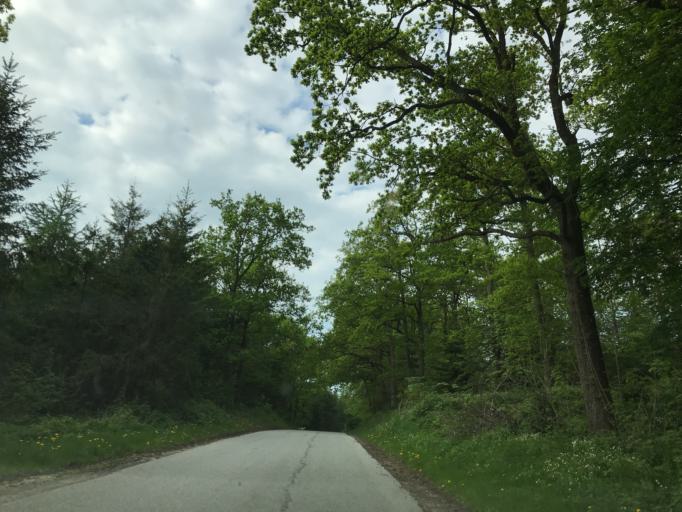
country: DK
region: South Denmark
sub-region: Assens Kommune
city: Assens
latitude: 55.3349
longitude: 9.9114
